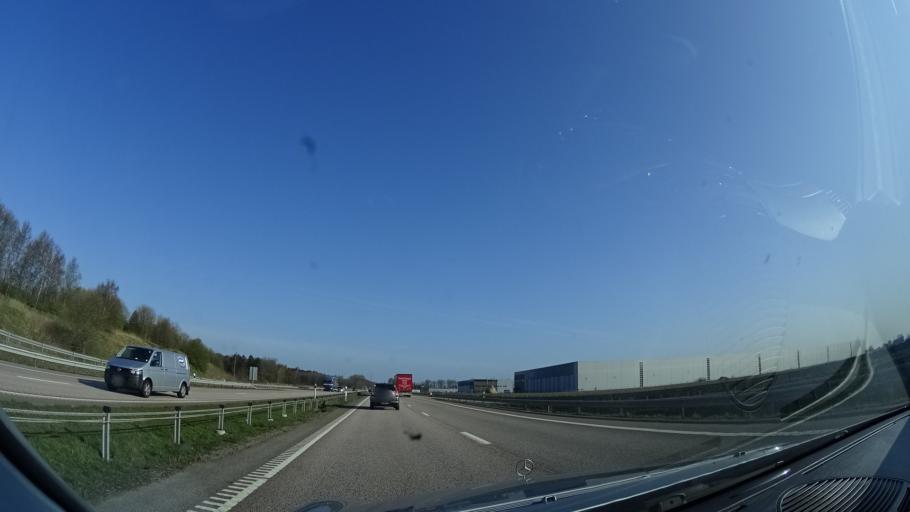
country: SE
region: Skane
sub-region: Helsingborg
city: Odakra
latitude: 56.0659
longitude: 12.7802
